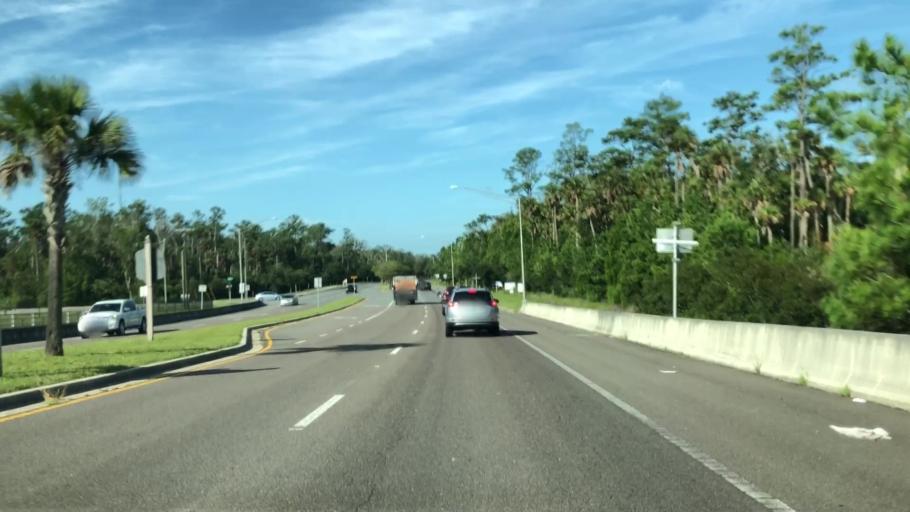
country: US
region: Florida
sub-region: Saint Johns County
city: Palm Valley
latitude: 30.1302
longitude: -81.3898
